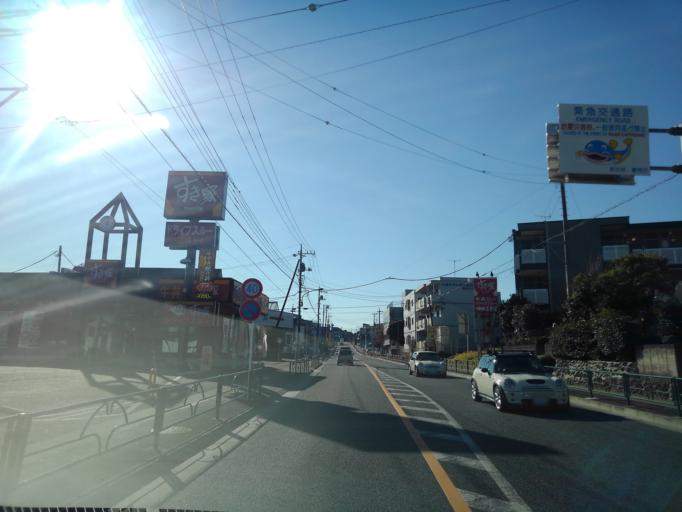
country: JP
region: Tokyo
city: Hino
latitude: 35.6891
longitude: 139.3706
